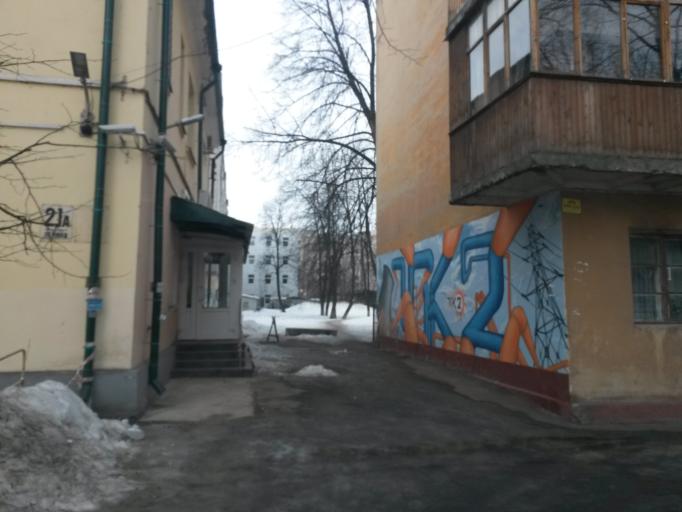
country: RU
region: Jaroslavl
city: Yaroslavl
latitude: 57.6377
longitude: 39.8720
